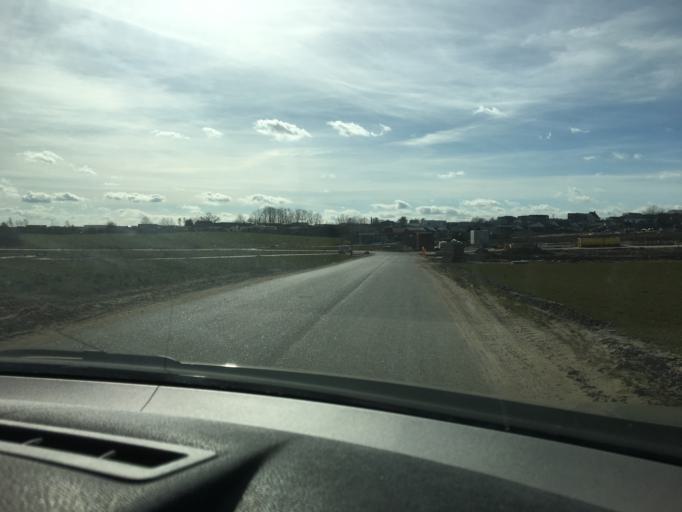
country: DK
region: South Denmark
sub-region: Vejle Kommune
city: Vejle
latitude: 55.7331
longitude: 9.6146
